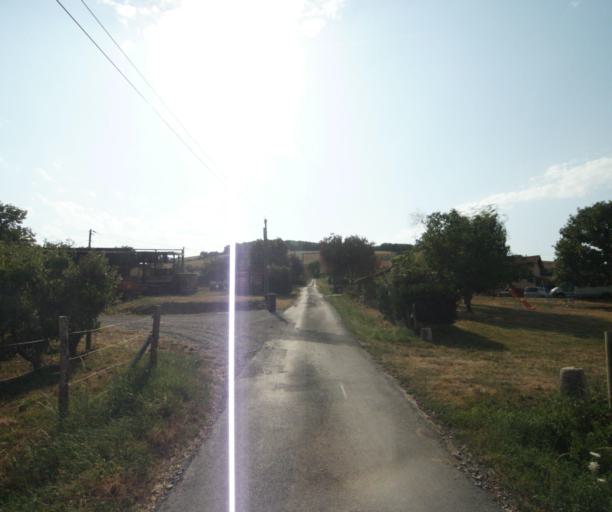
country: FR
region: Rhone-Alpes
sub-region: Departement du Rhone
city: Savigny
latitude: 45.8304
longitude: 4.5740
